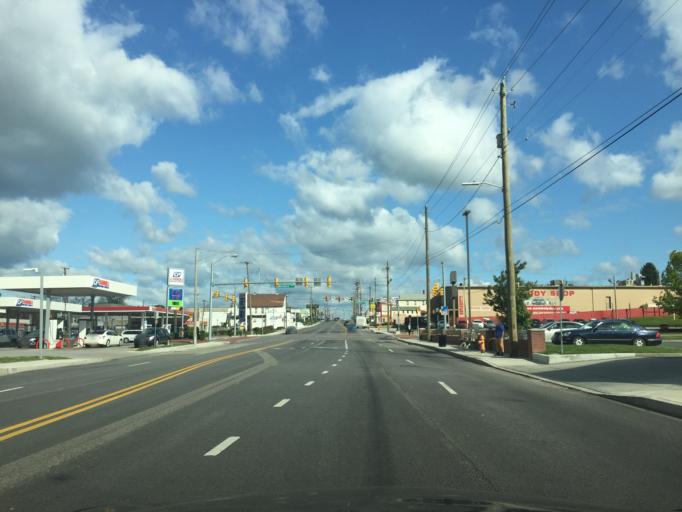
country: US
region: Maryland
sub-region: Baltimore County
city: Lochearn
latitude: 39.3480
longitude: -76.6908
